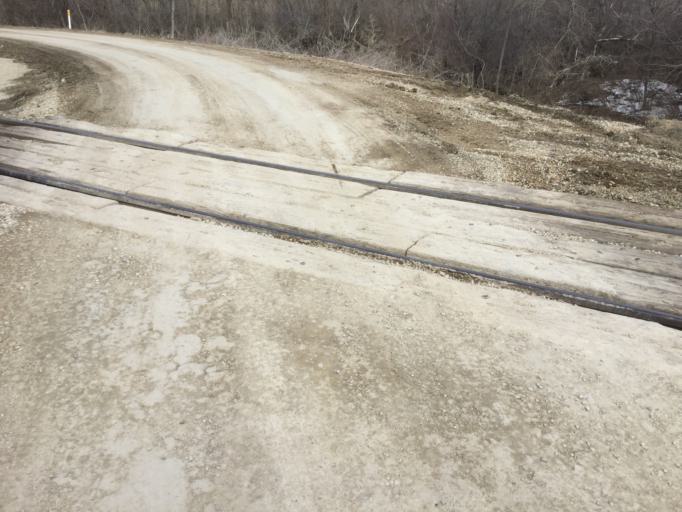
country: US
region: Kansas
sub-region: Osage County
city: Carbondale
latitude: 38.8340
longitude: -95.6964
